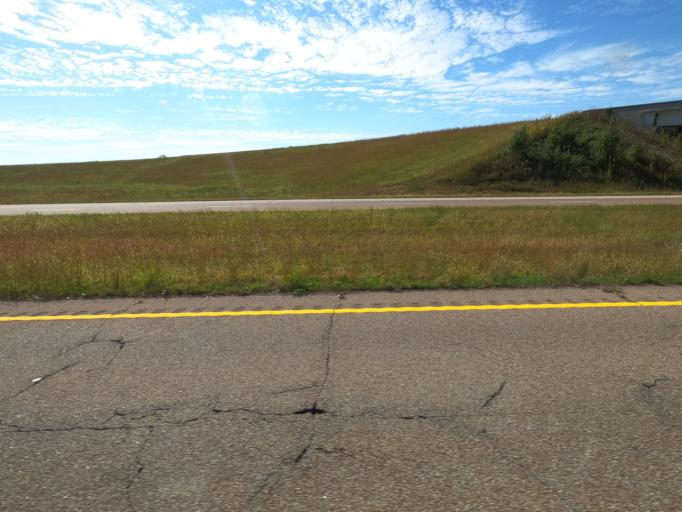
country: US
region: Tennessee
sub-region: Crockett County
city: Alamo
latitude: 35.7752
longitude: -89.1277
